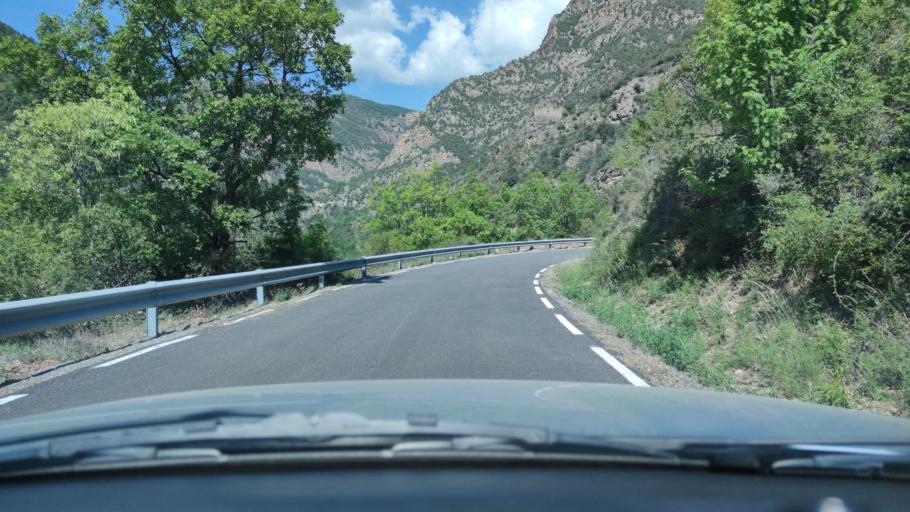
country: ES
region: Catalonia
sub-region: Provincia de Lleida
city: Coll de Nargo
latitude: 42.2952
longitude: 1.3129
